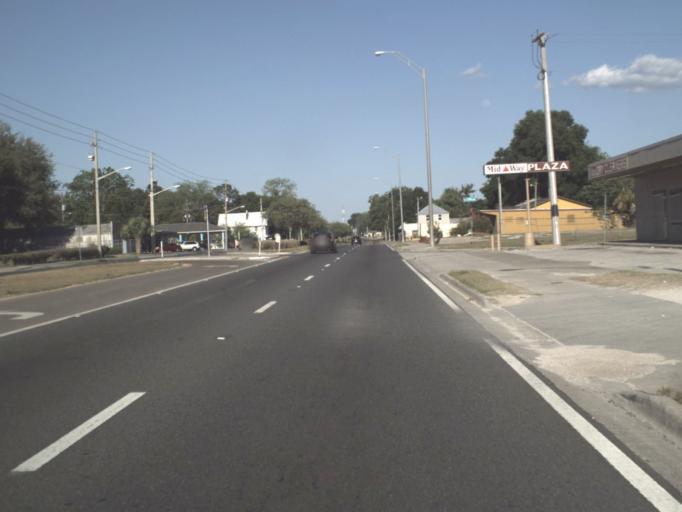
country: US
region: Florida
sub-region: Marion County
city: Ocala
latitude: 29.1861
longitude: -82.1591
